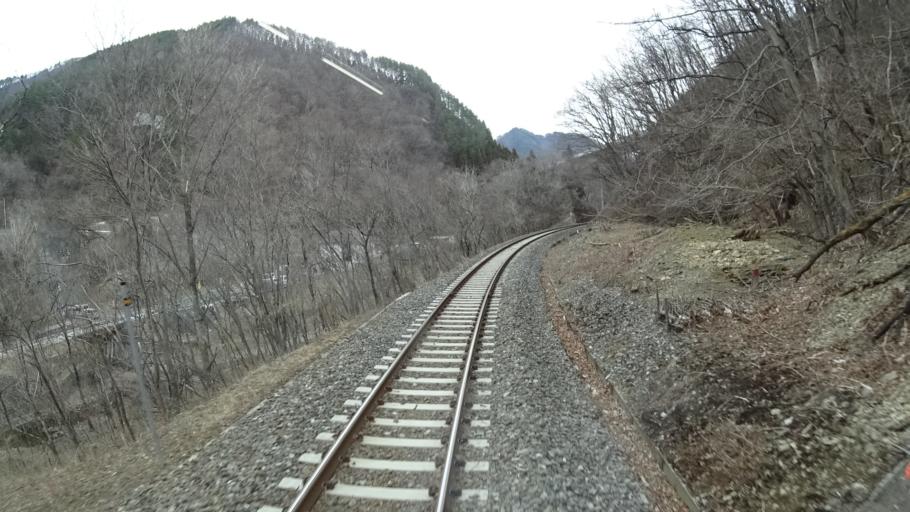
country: JP
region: Iwate
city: Kamaishi
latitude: 39.2946
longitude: 141.8642
